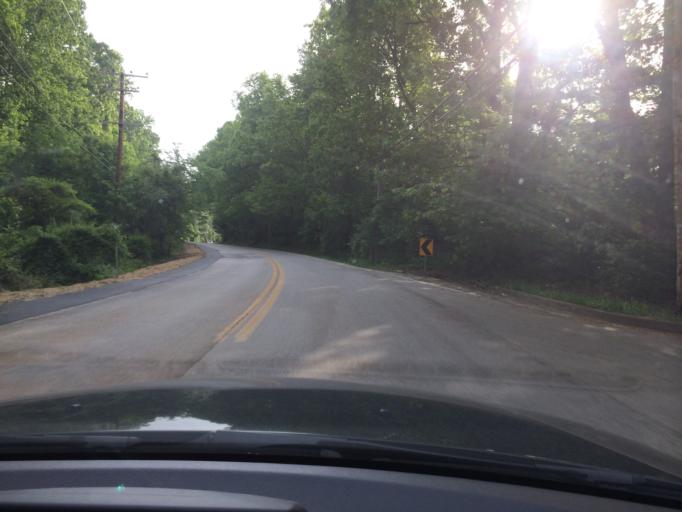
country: US
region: Maryland
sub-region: Howard County
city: Riverside
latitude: 39.1876
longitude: -76.9173
